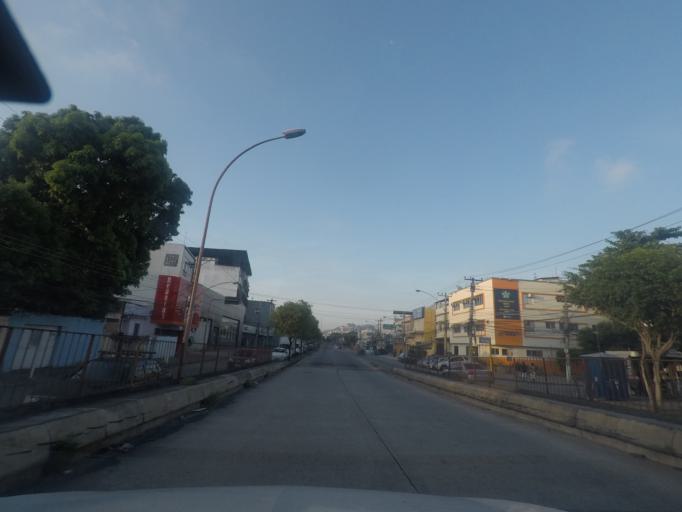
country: BR
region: Rio de Janeiro
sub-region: Duque De Caxias
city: Duque de Caxias
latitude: -22.8278
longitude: -43.2756
